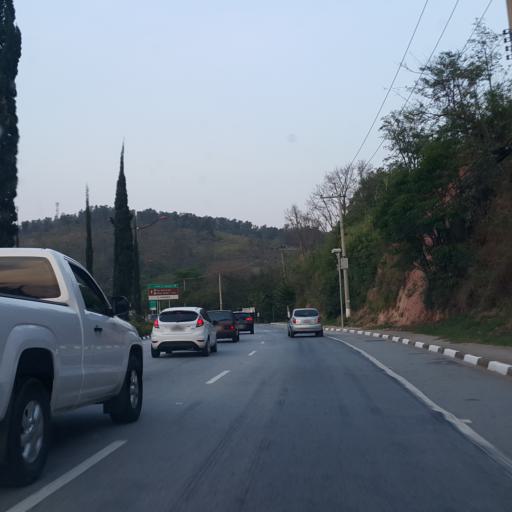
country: BR
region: Sao Paulo
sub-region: Vinhedo
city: Vinhedo
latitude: -23.0542
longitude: -46.9883
